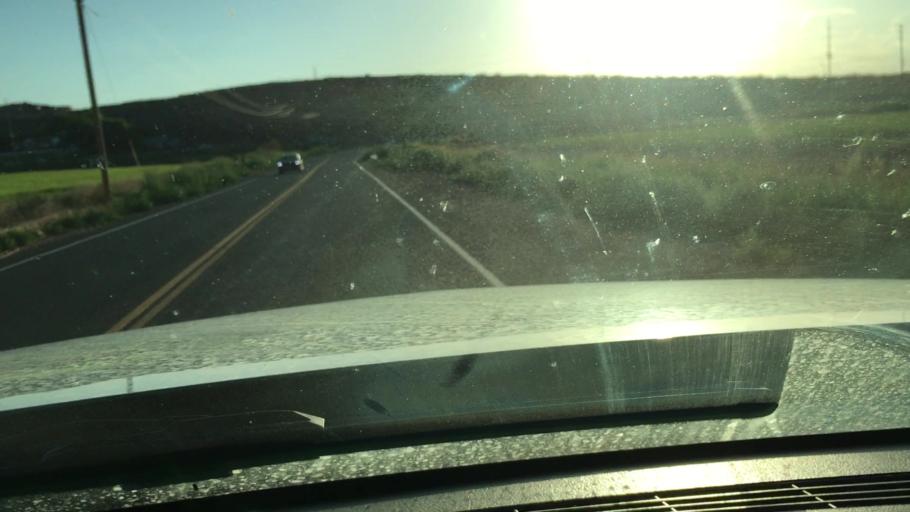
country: US
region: Utah
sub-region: Washington County
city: Washington
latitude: 37.0816
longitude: -113.5211
